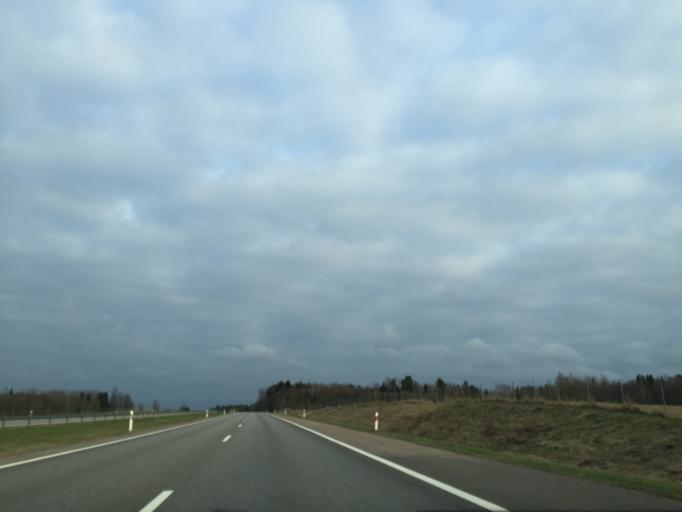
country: LT
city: Rietavas
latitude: 55.6740
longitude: 21.7169
